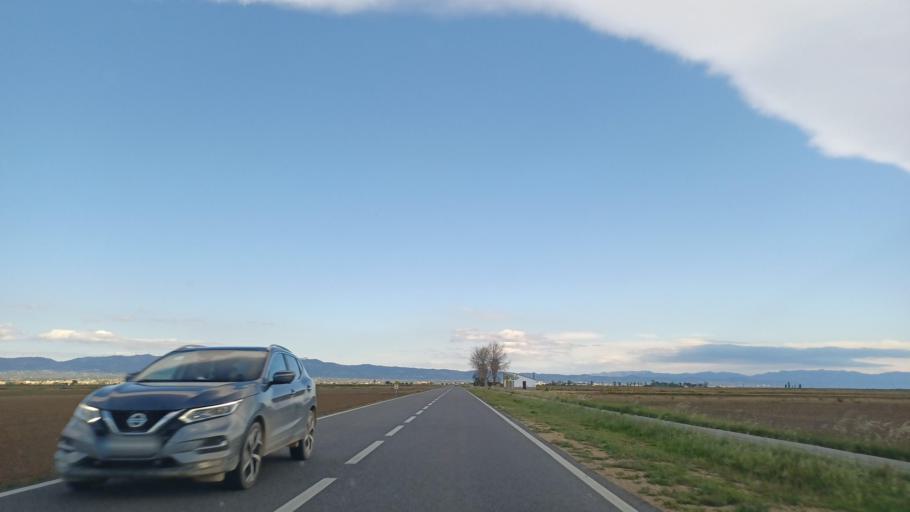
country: ES
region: Catalonia
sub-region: Provincia de Tarragona
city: Deltebre
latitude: 40.7413
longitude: 0.7123
